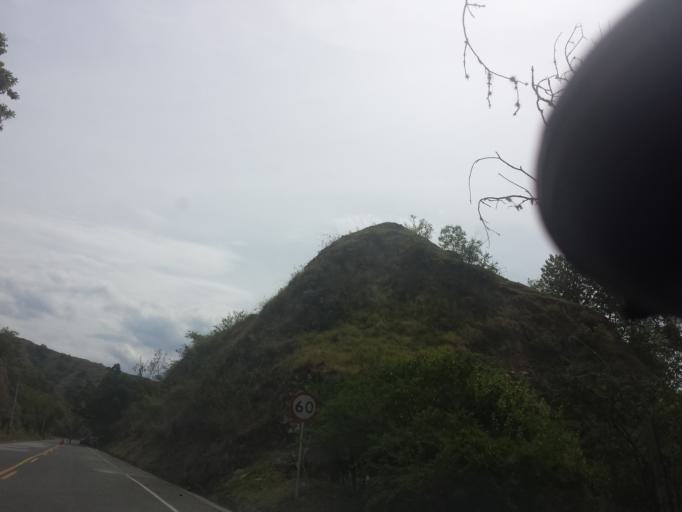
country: CO
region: Antioquia
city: Antioquia
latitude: 6.5711
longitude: -75.8395
